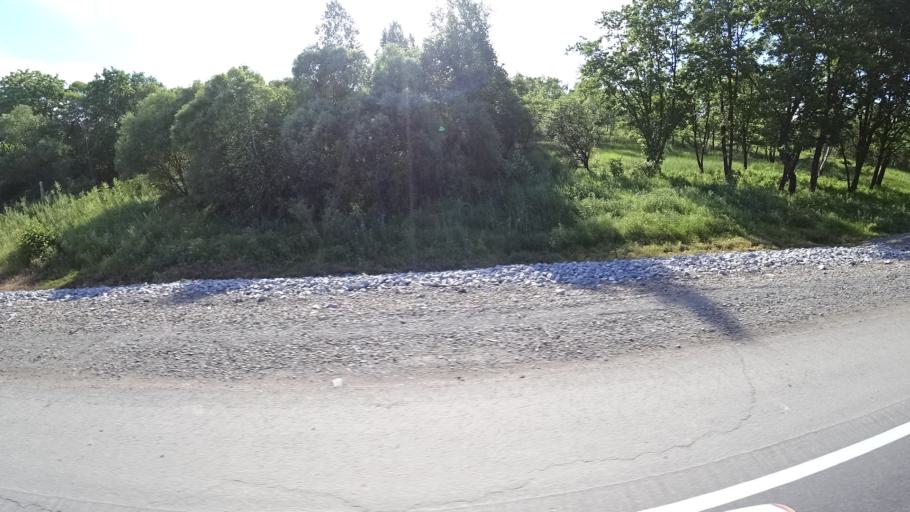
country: RU
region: Khabarovsk Krai
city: Khor
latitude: 47.8572
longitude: 134.9623
